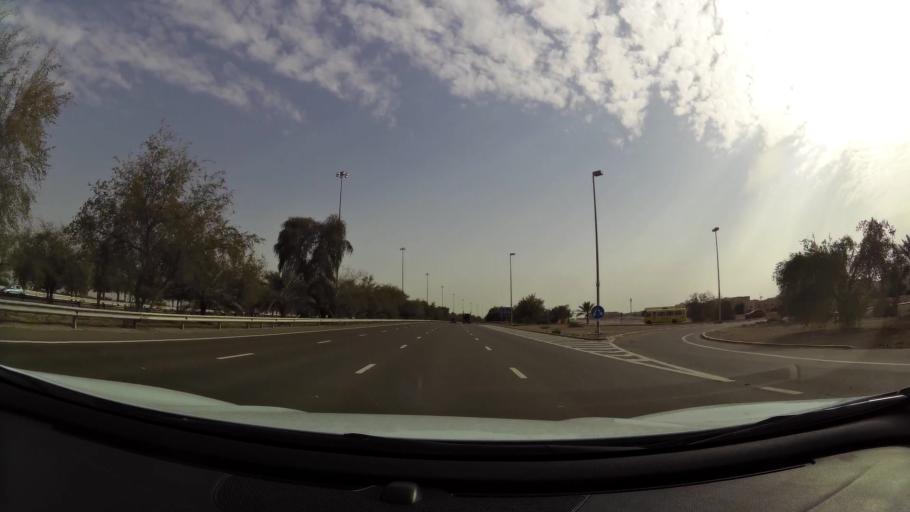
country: AE
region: Abu Dhabi
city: Abu Dhabi
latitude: 24.4540
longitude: 54.6783
